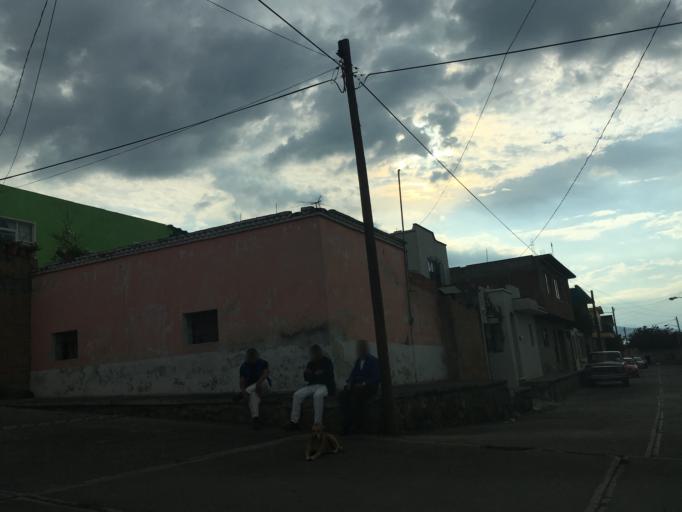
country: MX
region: Michoacan
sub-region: Morelia
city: Morelos
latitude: 19.6516
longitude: -101.2388
